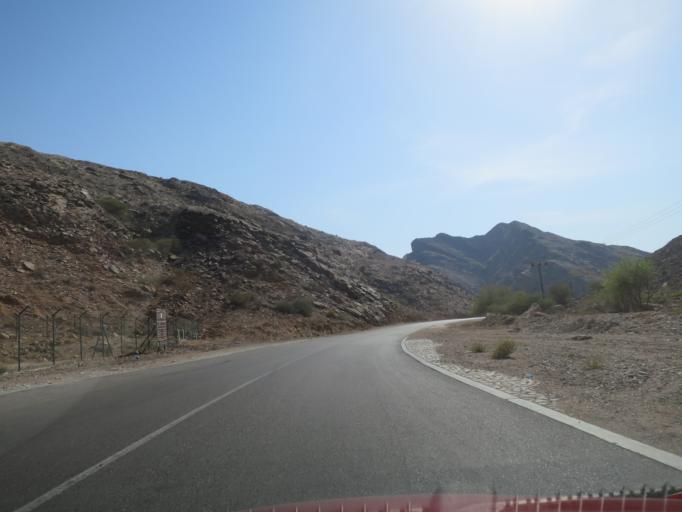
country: OM
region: Muhafazat Masqat
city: Muscat
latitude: 23.5102
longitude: 58.6763
